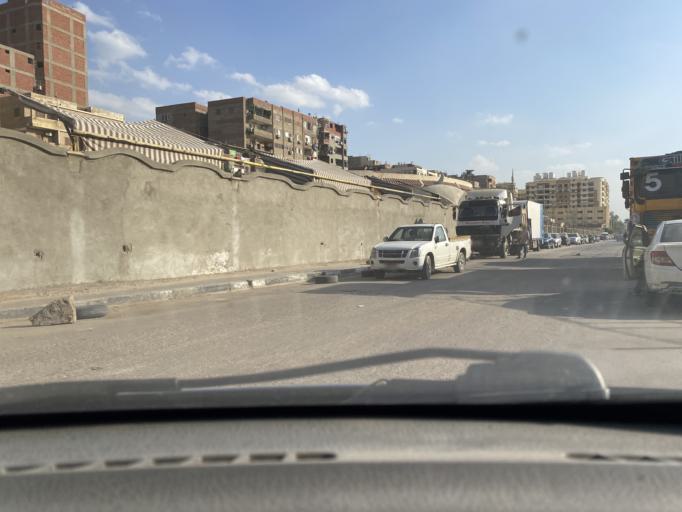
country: EG
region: Muhafazat al Qahirah
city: Cairo
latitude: 30.1064
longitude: 31.3055
